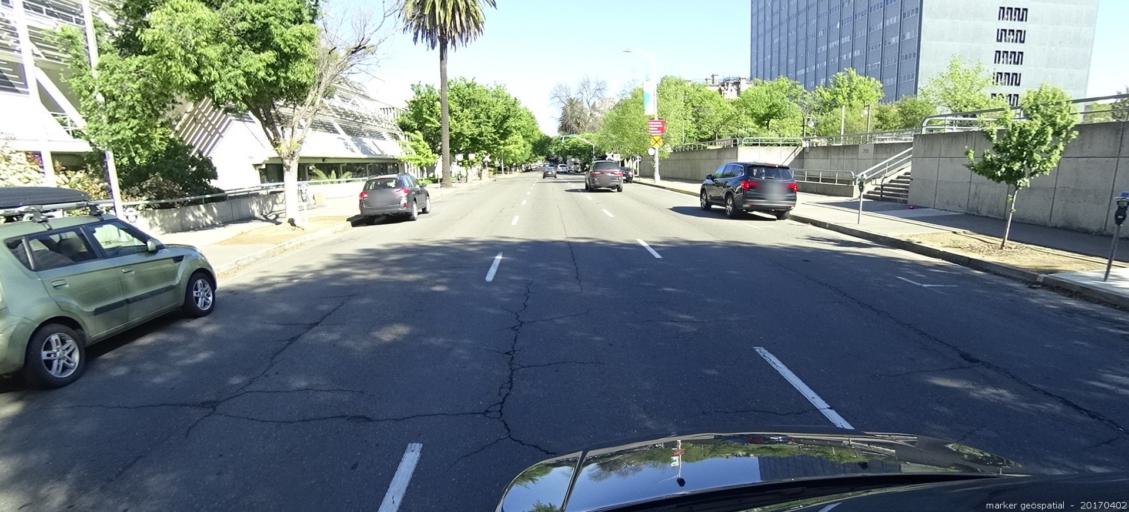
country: US
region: California
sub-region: Sacramento County
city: Sacramento
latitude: 38.5769
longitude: -121.4991
